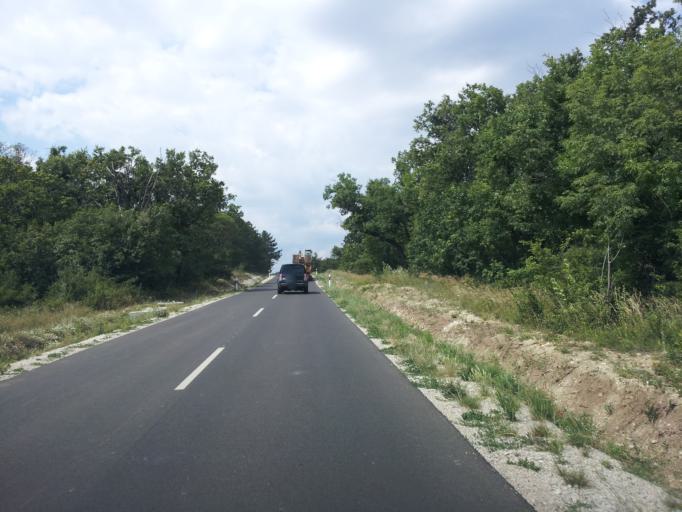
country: HU
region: Veszprem
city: Zanka
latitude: 46.8929
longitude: 17.7411
